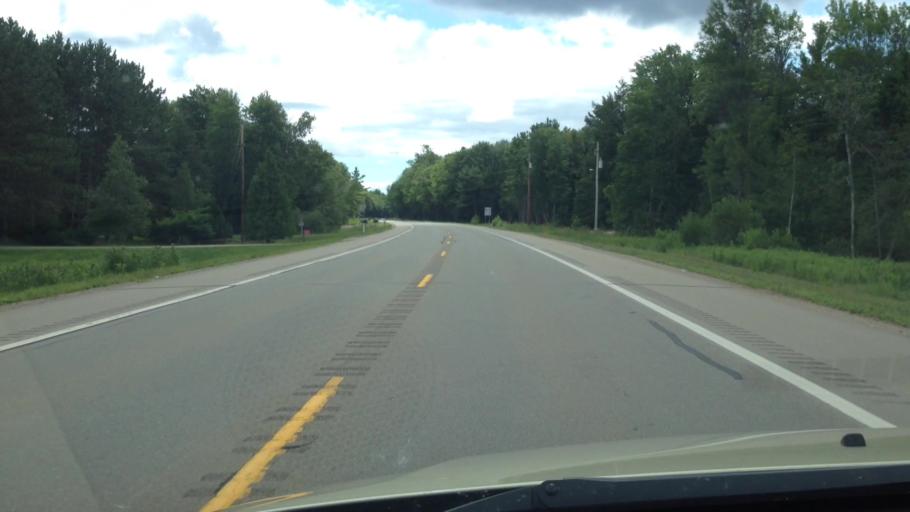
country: US
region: Michigan
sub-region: Menominee County
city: Menominee
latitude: 45.3050
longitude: -87.4395
